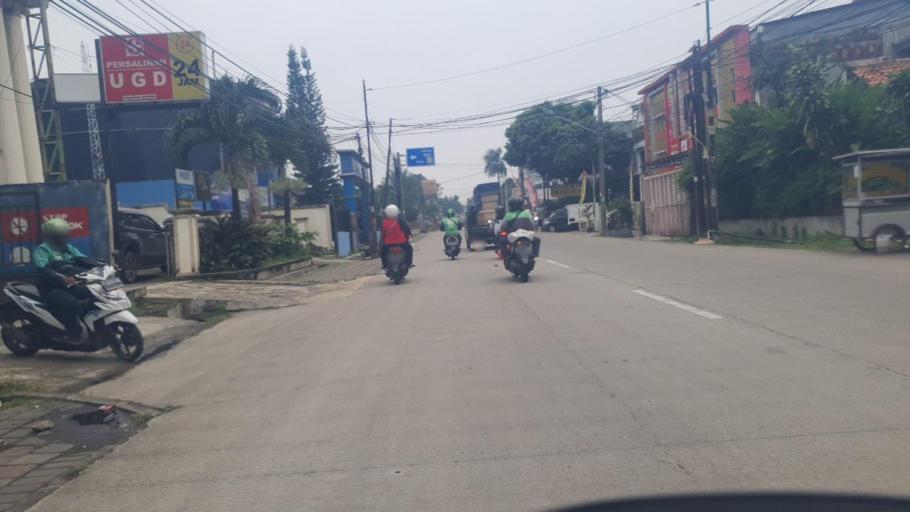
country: ID
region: West Java
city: Bogor
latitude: -6.5881
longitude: 106.7878
